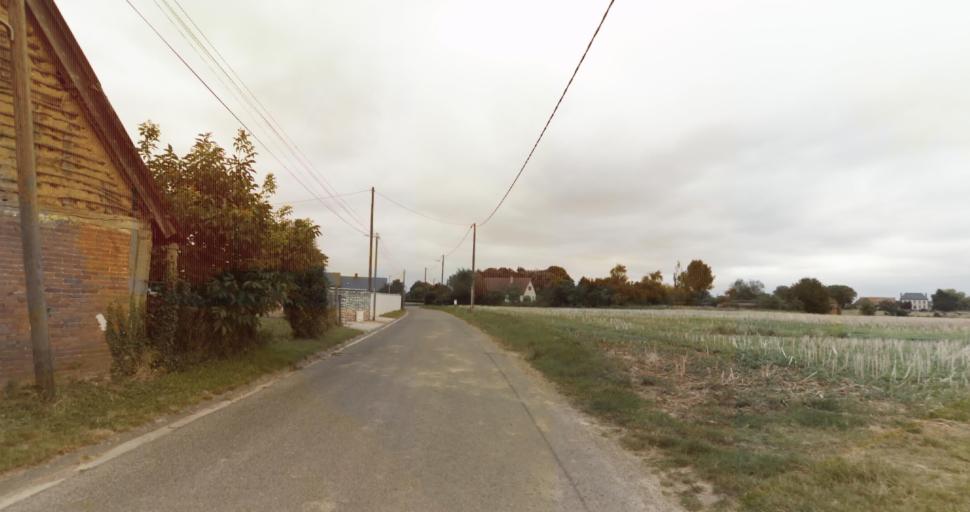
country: FR
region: Haute-Normandie
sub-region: Departement de l'Eure
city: La Couture-Boussey
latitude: 48.9276
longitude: 1.3252
